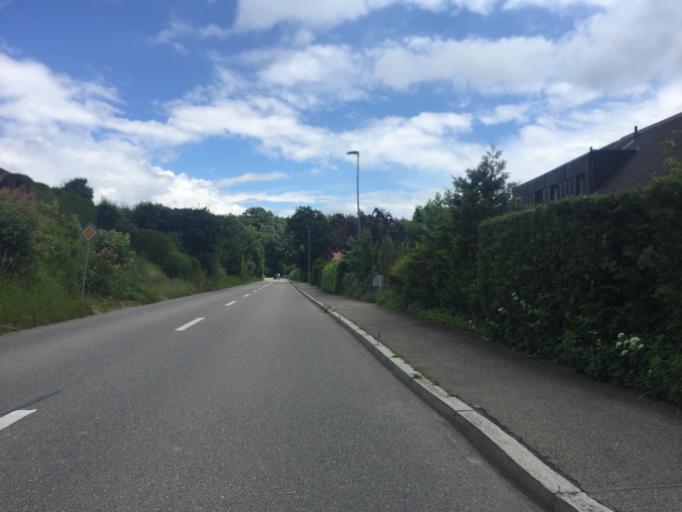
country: CH
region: Bern
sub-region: Bern-Mittelland District
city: Wohlen
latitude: 46.9737
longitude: 7.3588
